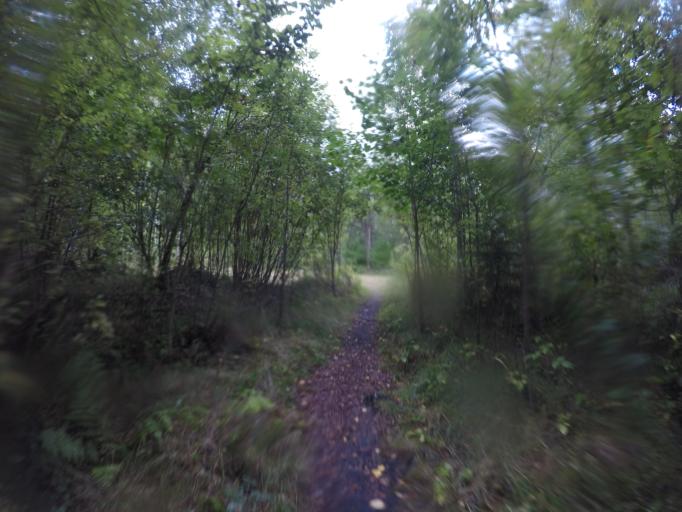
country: SE
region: Vaestmanland
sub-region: Vasteras
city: Vasteras
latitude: 59.6452
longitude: 16.5178
